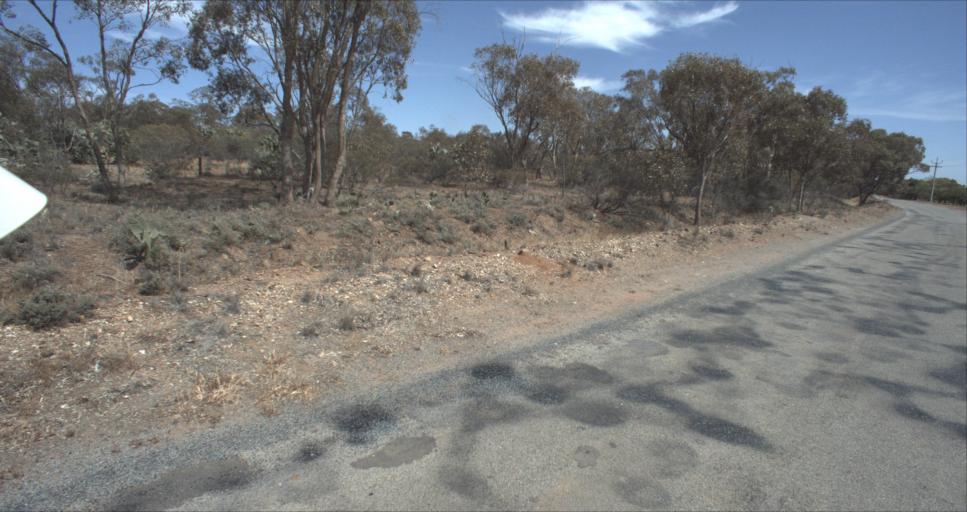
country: AU
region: New South Wales
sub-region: Leeton
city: Leeton
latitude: -34.5637
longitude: 146.4616
